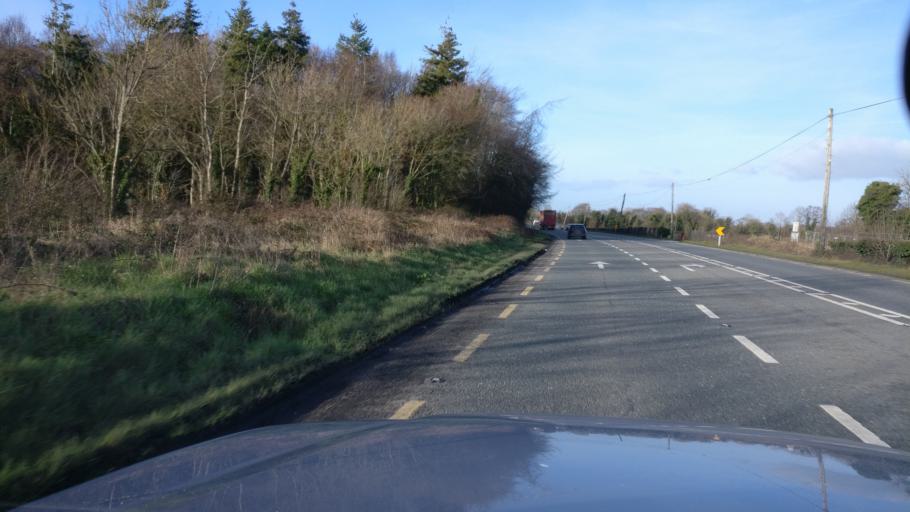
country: IE
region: Leinster
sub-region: Uibh Fhaili
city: Tullamore
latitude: 53.2312
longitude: -7.4756
